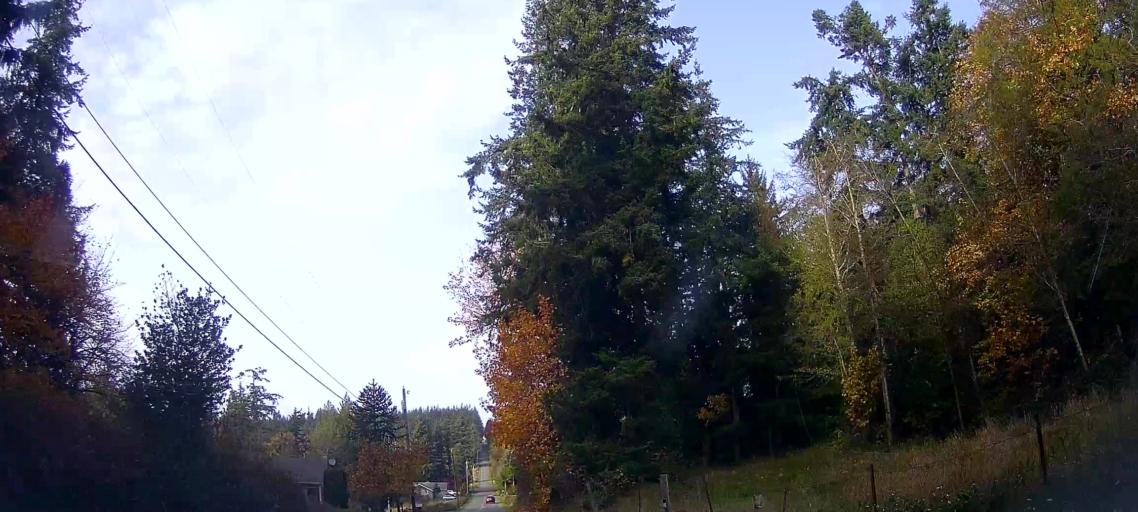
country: US
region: Washington
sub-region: Snohomish County
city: Stanwood
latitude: 48.2560
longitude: -122.3414
